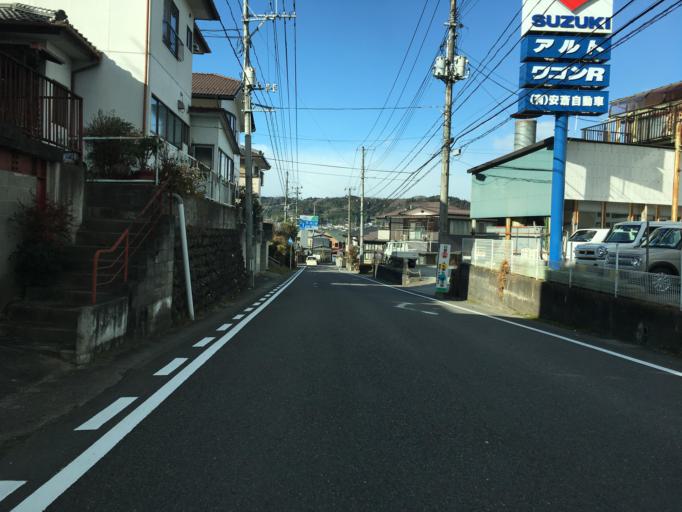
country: JP
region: Fukushima
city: Nihommatsu
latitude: 37.5974
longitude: 140.4507
